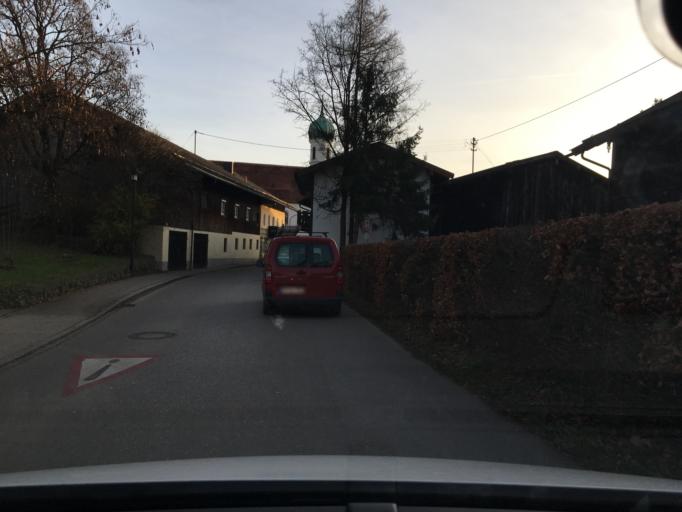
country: DE
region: Bavaria
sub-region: Upper Bavaria
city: Raubling
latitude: 47.8049
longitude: 12.1167
